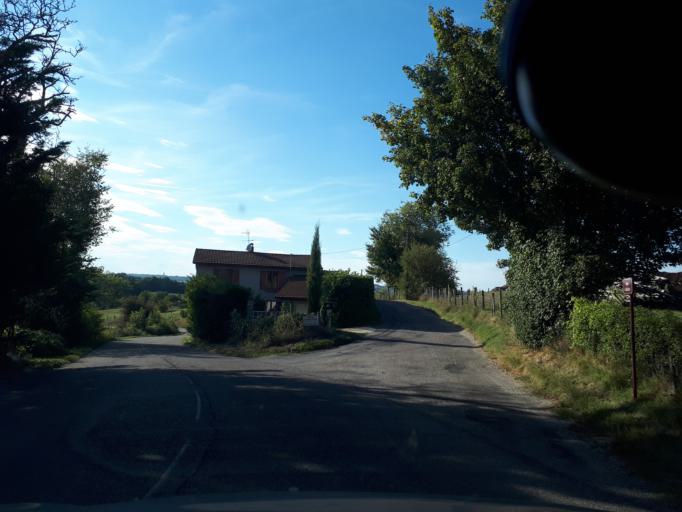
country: FR
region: Rhone-Alpes
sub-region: Departement de l'Isere
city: Maubec
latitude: 45.5379
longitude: 5.2587
